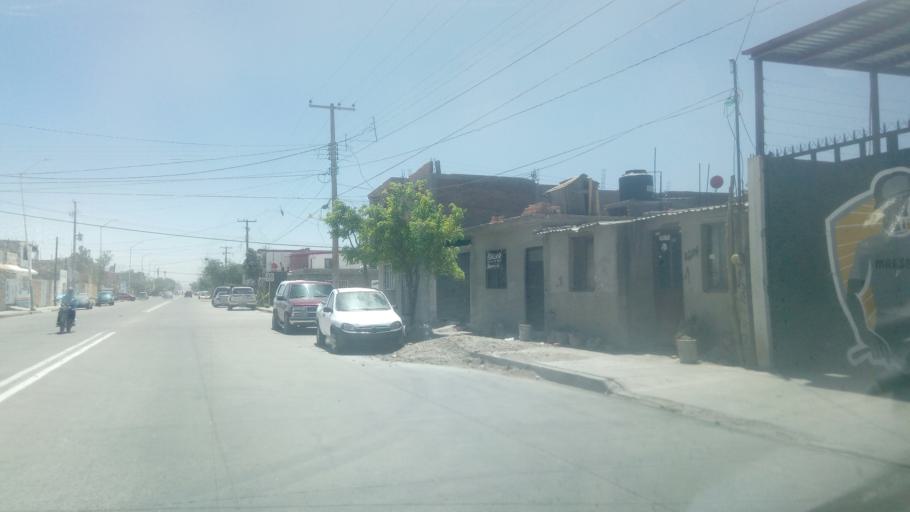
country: MX
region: Durango
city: Victoria de Durango
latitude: 24.0174
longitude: -104.6264
